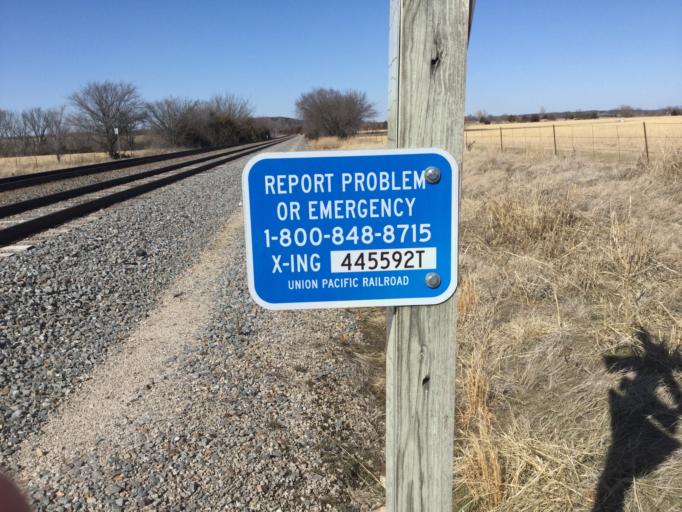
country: US
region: Kansas
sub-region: Wilson County
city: Neodesha
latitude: 37.5446
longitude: -95.6640
